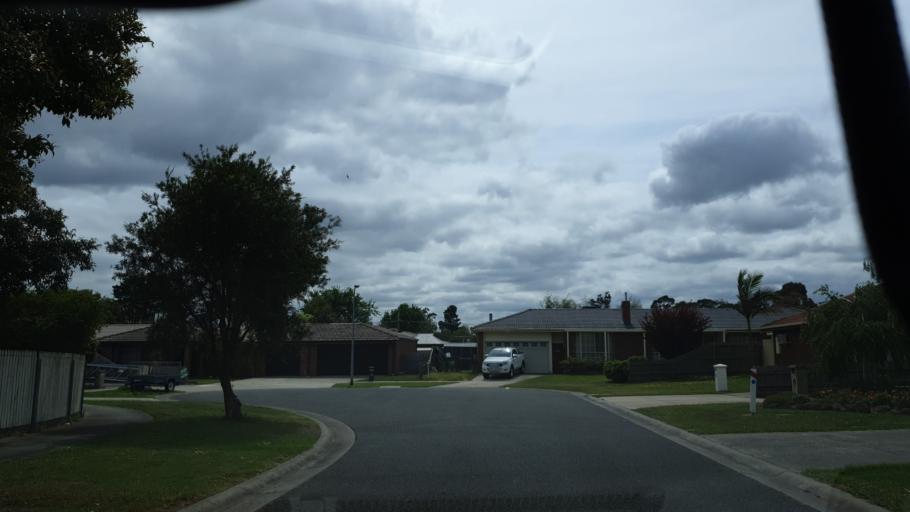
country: AU
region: Victoria
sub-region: Casey
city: Cranbourne North
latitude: -38.0774
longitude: 145.2776
